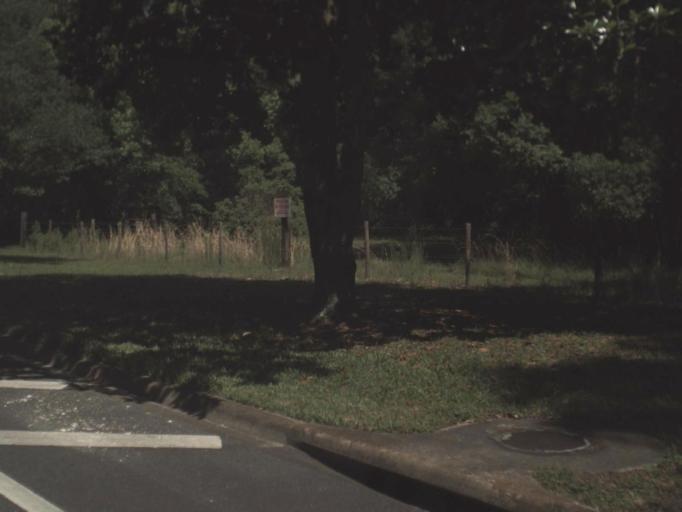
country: US
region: Florida
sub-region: Clay County
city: Asbury Lake
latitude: 29.9826
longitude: -81.8016
